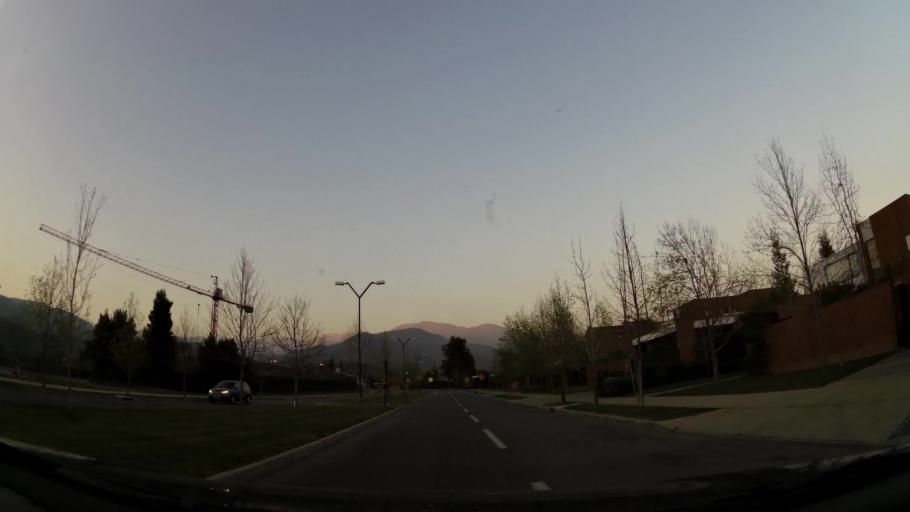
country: CL
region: Santiago Metropolitan
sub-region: Provincia de Chacabuco
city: Chicureo Abajo
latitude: -33.3311
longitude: -70.5491
